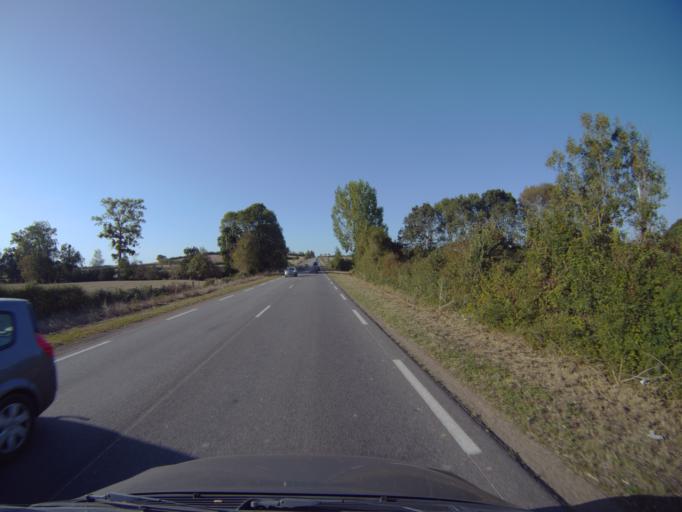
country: FR
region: Pays de la Loire
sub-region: Departement de la Vendee
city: Angles
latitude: 46.4382
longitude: -1.4041
